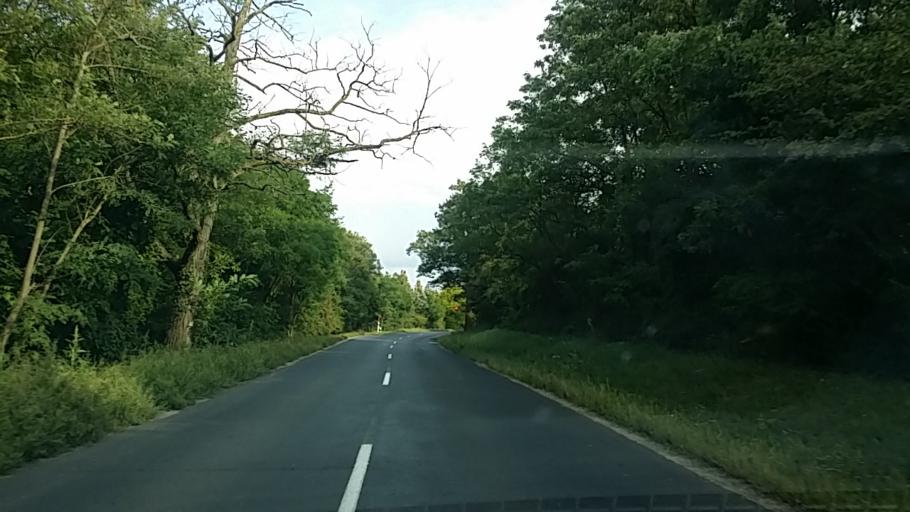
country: HU
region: Gyor-Moson-Sopron
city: Sopron
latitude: 47.6756
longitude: 16.6272
